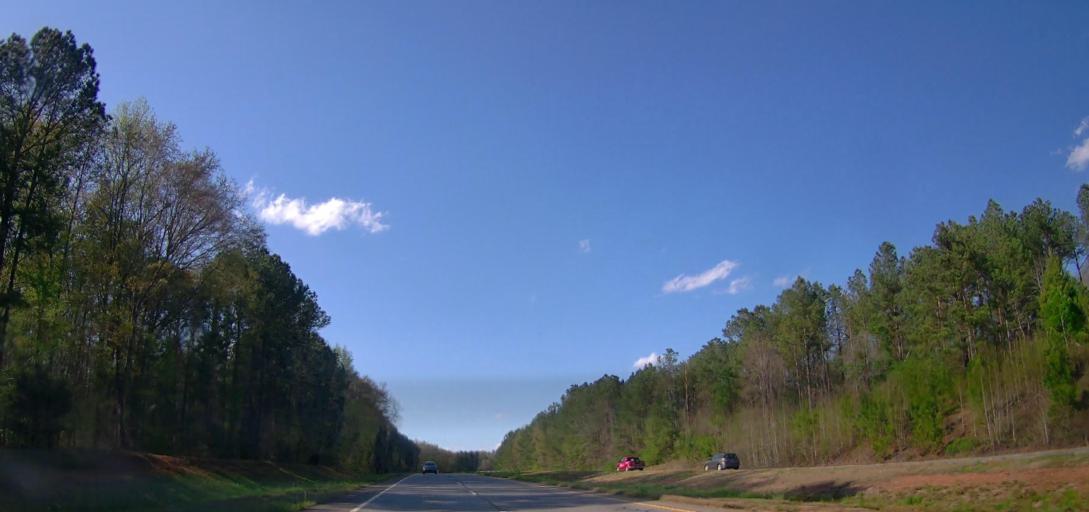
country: US
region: Georgia
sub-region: Baldwin County
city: Hardwick
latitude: 33.0387
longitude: -83.2535
